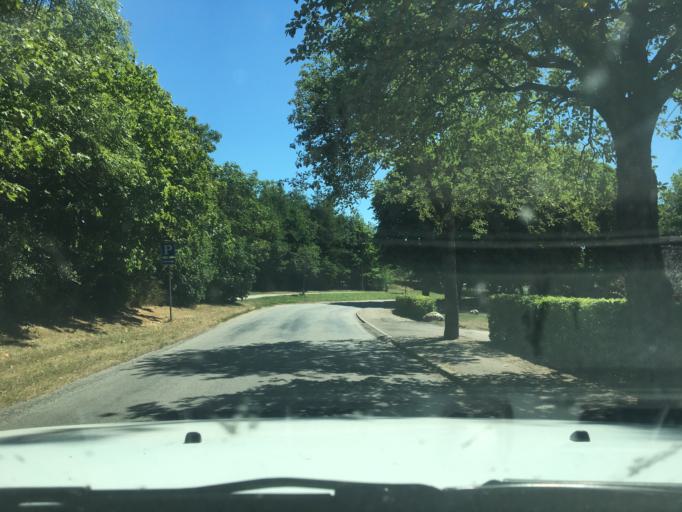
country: DK
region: Central Jutland
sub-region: Syddjurs Kommune
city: Hornslet
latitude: 56.3324
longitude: 10.3760
